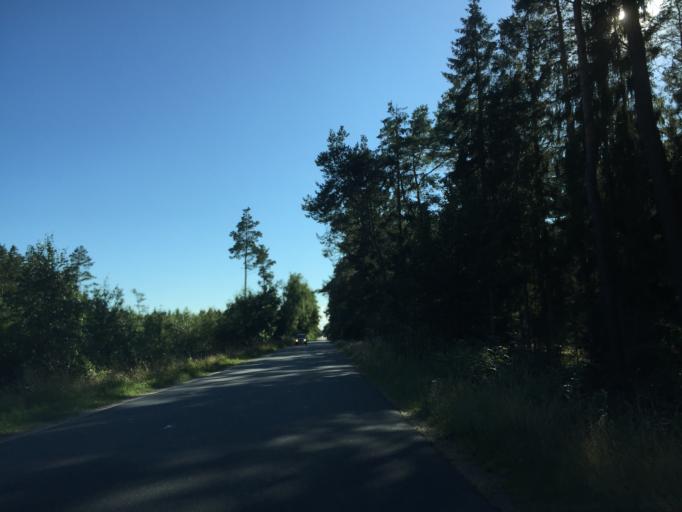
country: DK
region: Central Jutland
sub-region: Silkeborg Kommune
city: Svejbaek
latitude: 56.2088
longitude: 9.6782
